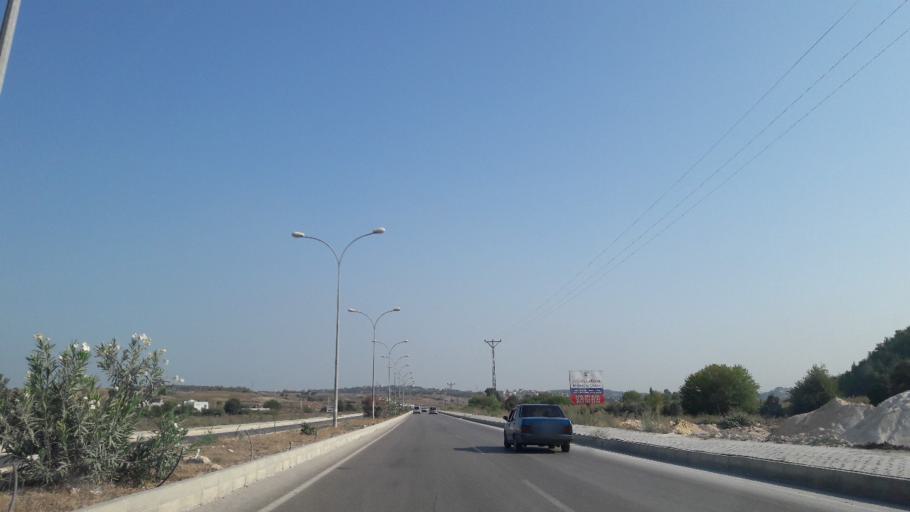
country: TR
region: Adana
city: Yuregir
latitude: 37.0574
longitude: 35.4423
